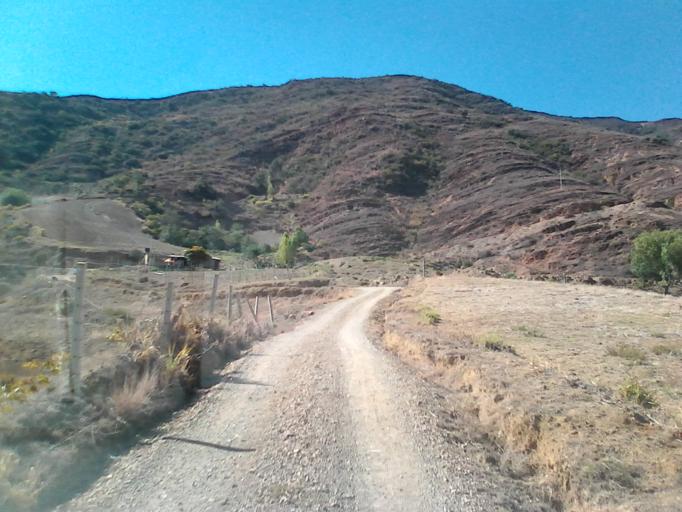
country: CO
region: Boyaca
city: Sachica
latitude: 5.5565
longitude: -73.5498
